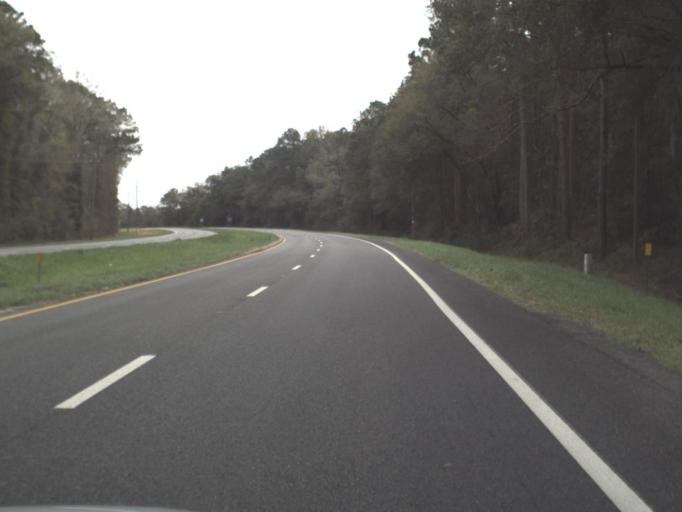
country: US
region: Florida
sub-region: Gadsden County
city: Midway
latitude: 30.5397
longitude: -84.3707
